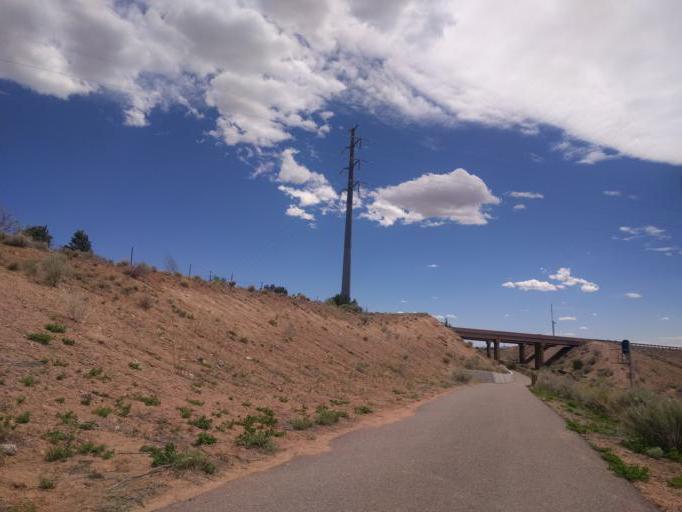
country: US
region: New Mexico
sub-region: Santa Fe County
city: Santa Fe
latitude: 35.6330
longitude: -105.9643
